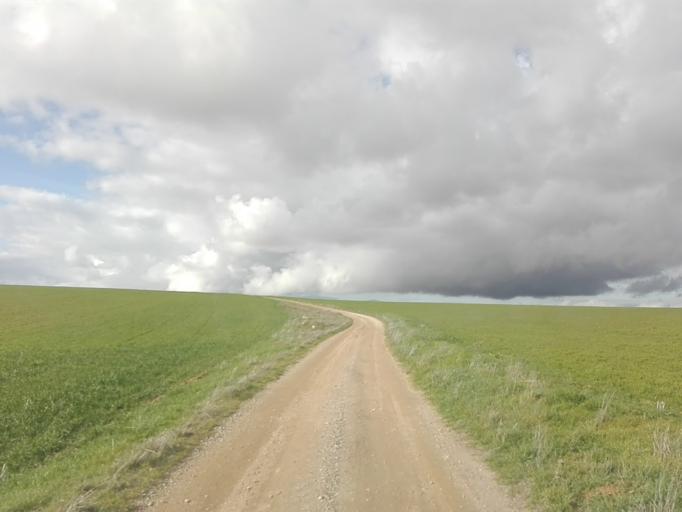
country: ES
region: Extremadura
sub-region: Provincia de Badajoz
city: Llerena
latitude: 38.2925
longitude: -5.9845
